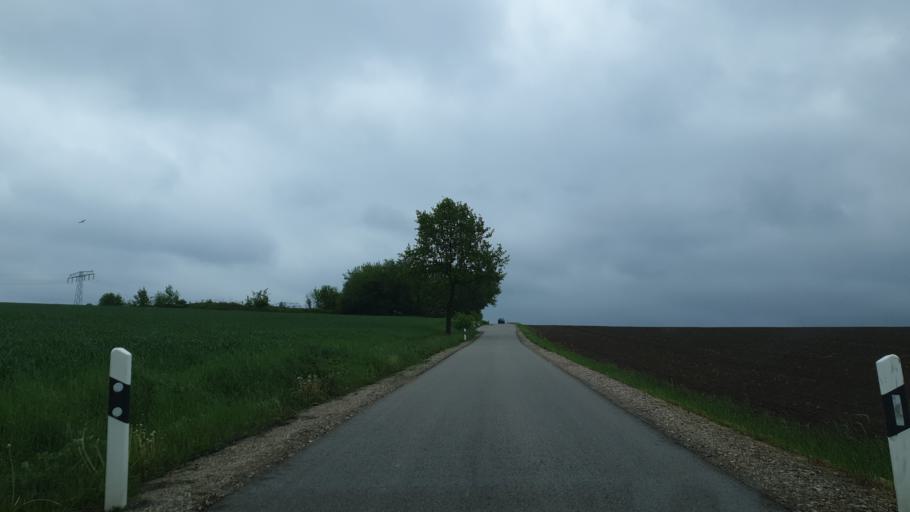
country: DE
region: Saxony
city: Limbach-Oberfrohna
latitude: 50.8547
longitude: 12.8051
